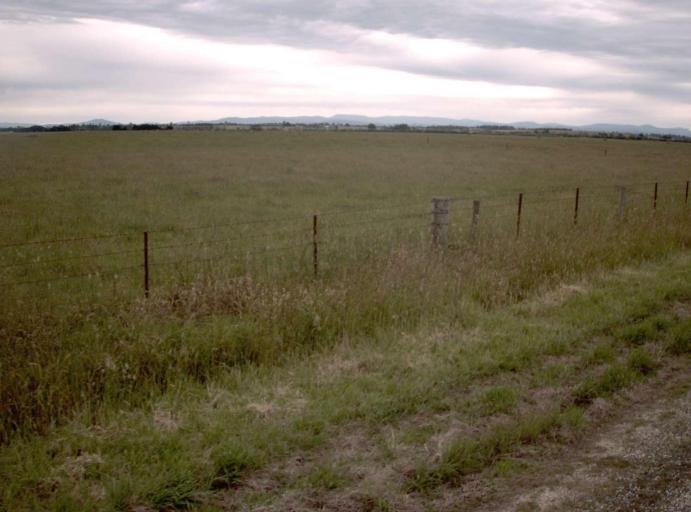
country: AU
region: Victoria
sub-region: Wellington
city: Sale
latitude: -38.0403
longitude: 147.1763
